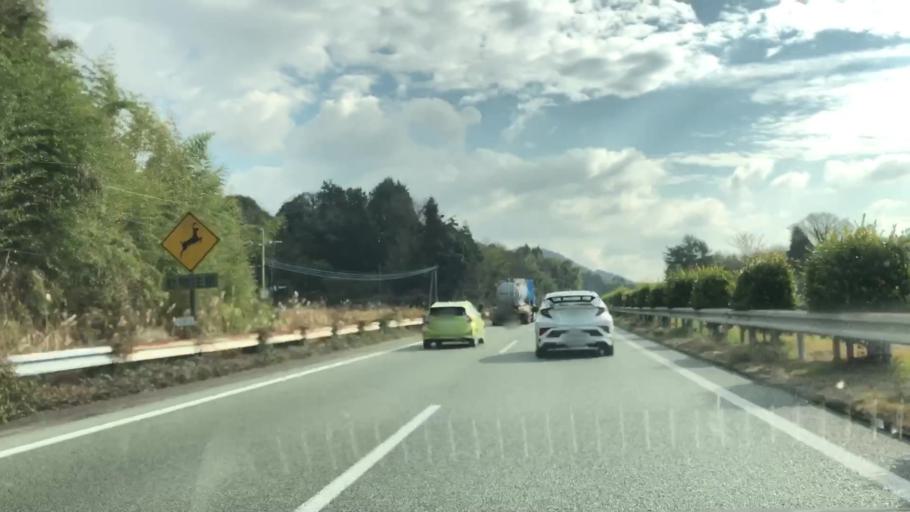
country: JP
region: Fukuoka
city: Setakamachi-takayanagi
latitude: 33.1107
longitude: 130.5319
